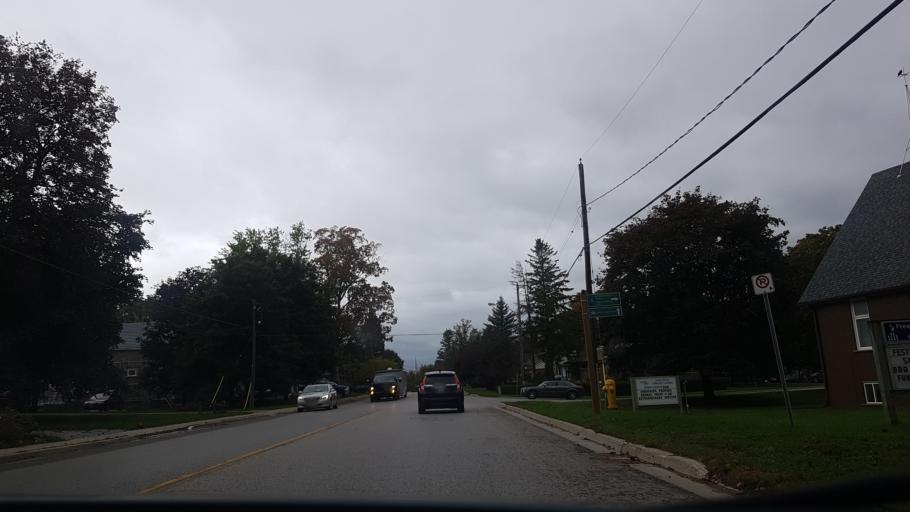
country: CA
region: Ontario
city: Uxbridge
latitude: 44.1051
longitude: -79.1146
